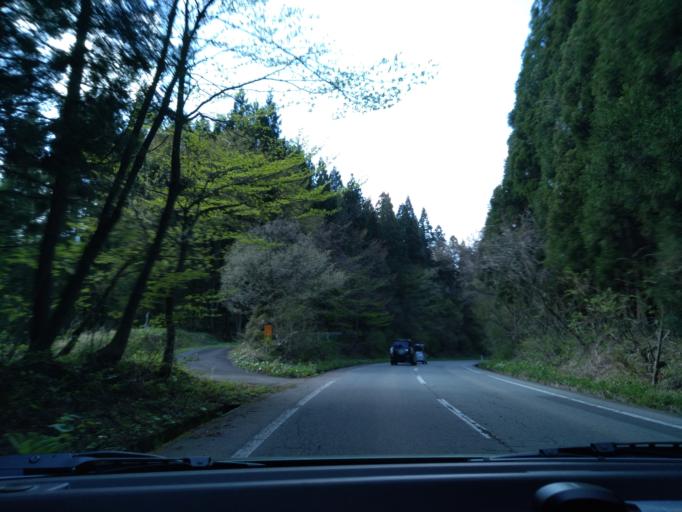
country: JP
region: Akita
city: Akita
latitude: 39.6895
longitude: 140.2756
